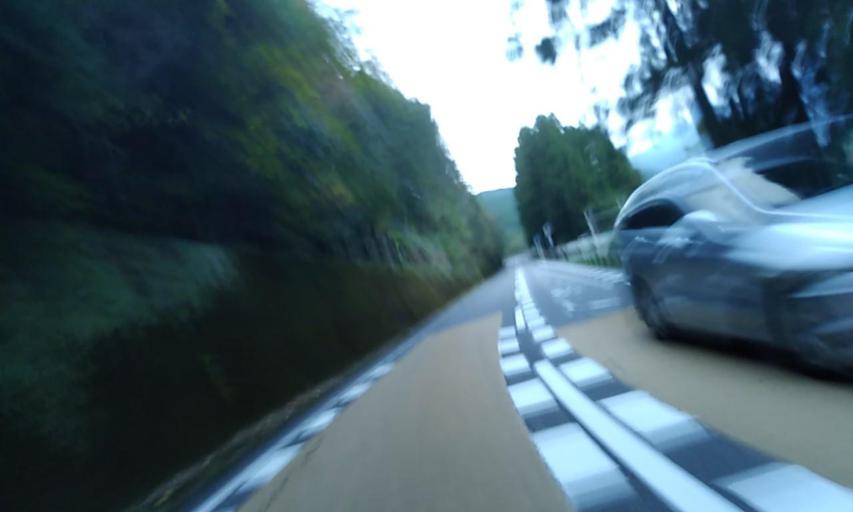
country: JP
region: Wakayama
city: Shingu
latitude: 33.7330
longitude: 135.9426
